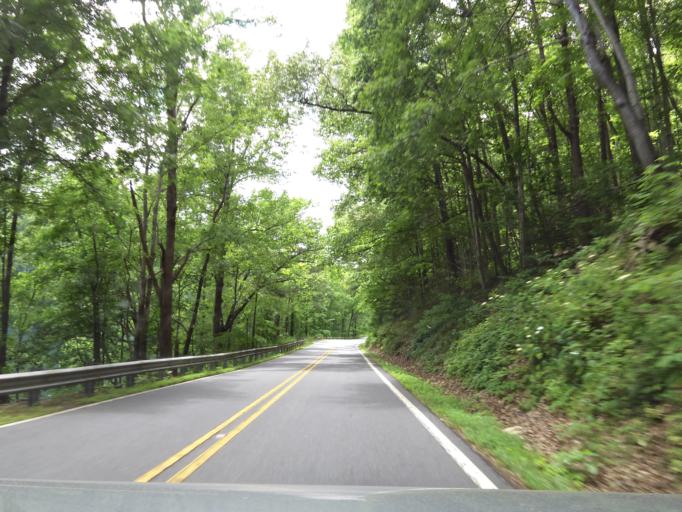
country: US
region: North Carolina
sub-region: Graham County
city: Robbinsville
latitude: 35.4532
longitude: -83.9267
